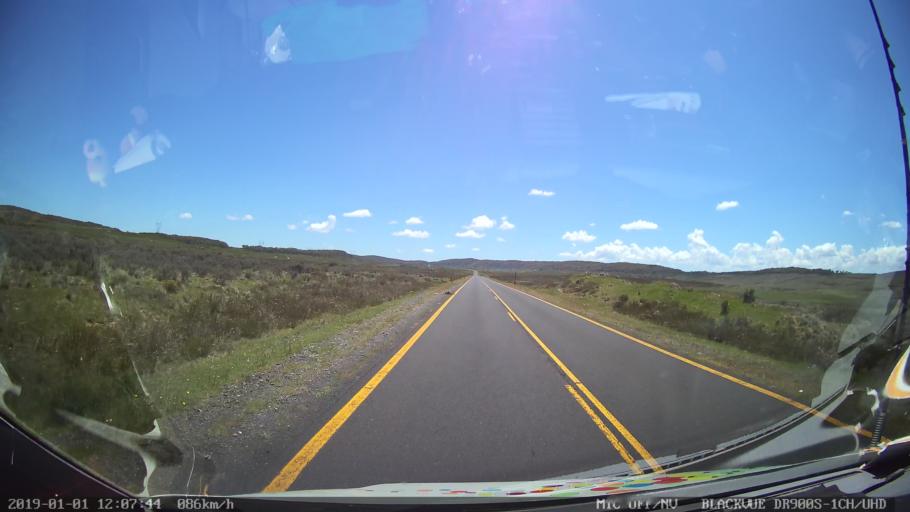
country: AU
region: New South Wales
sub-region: Tumut Shire
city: Tumut
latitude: -35.8291
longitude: 148.4912
